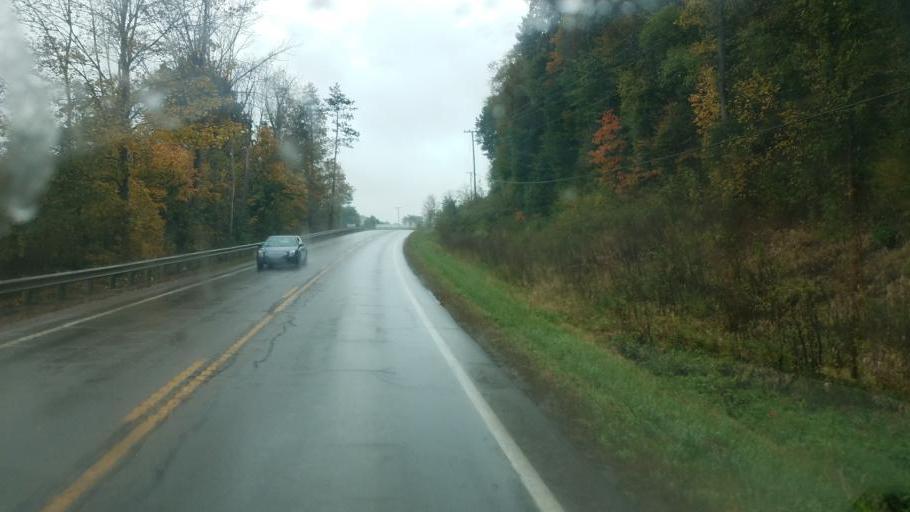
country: US
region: Ohio
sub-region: Holmes County
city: Millersburg
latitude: 40.6166
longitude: -81.9175
